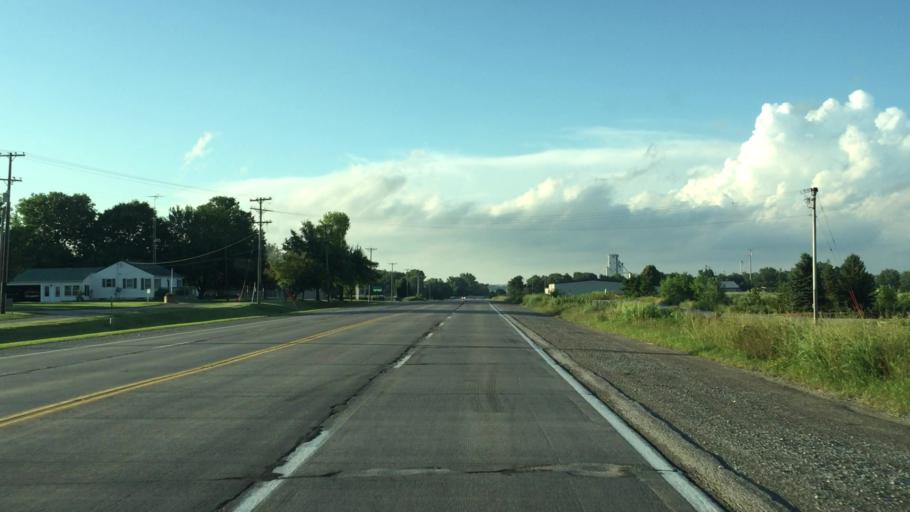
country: US
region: Iowa
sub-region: Johnson County
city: University Heights
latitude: 41.6209
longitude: -91.5447
